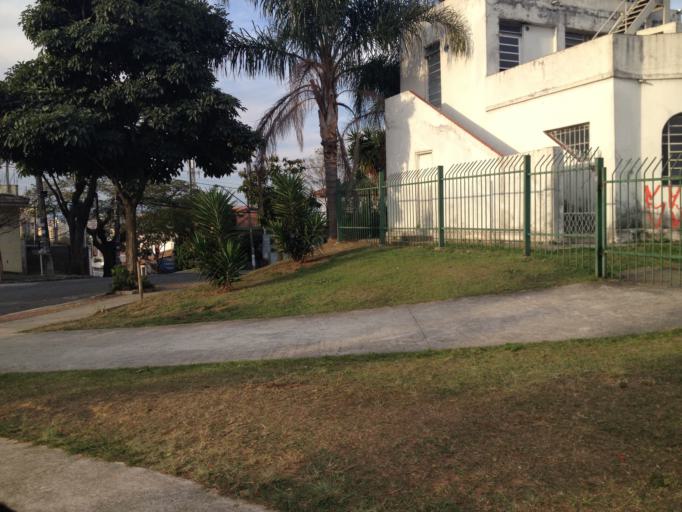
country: BR
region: Sao Paulo
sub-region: Sao Paulo
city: Sao Paulo
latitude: -23.4963
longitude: -46.6200
